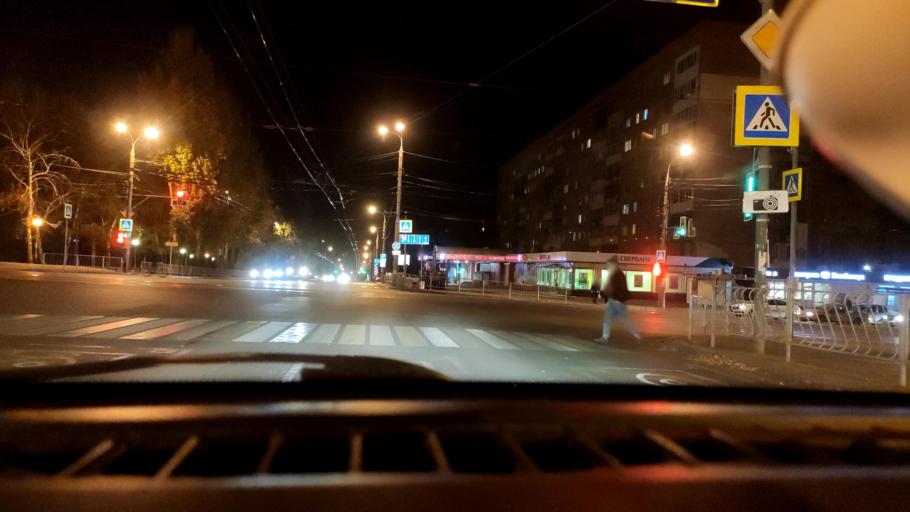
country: RU
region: Samara
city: Samara
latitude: 53.2347
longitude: 50.2201
